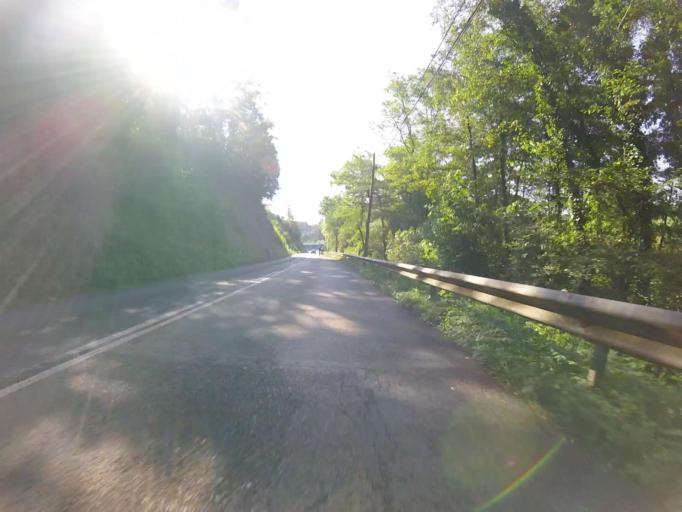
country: ES
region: Basque Country
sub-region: Provincia de Guipuzcoa
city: Asteasu
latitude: 43.1910
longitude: -2.0889
